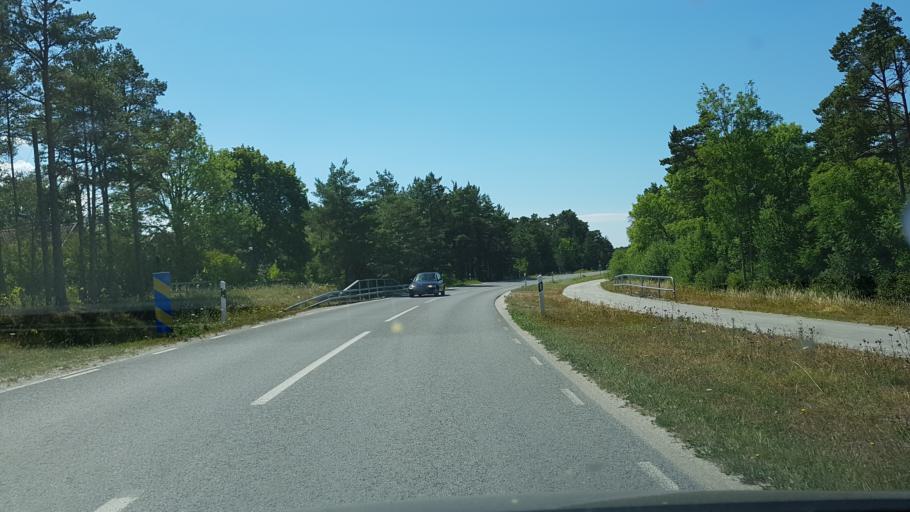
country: SE
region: Gotland
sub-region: Gotland
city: Visby
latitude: 57.6947
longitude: 18.3760
